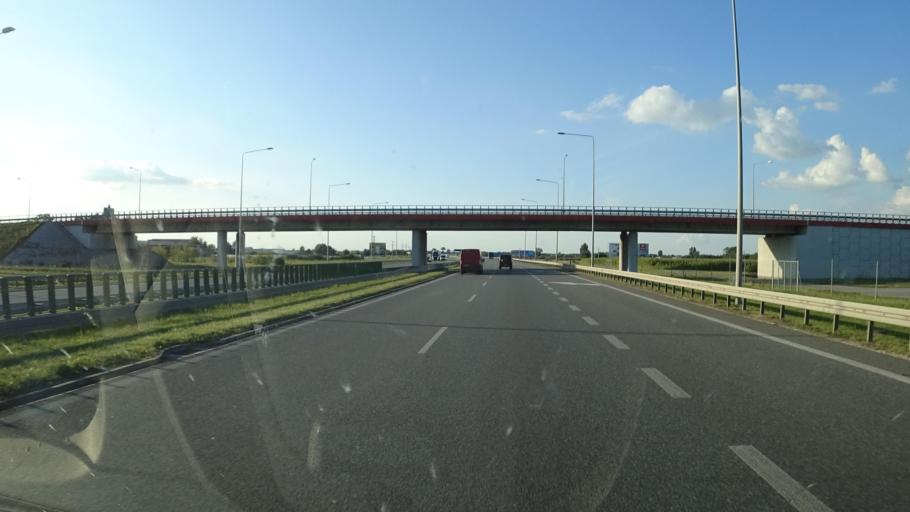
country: PL
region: Lodz Voivodeship
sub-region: Powiat leczycki
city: Piatek
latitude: 52.0677
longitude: 19.5359
